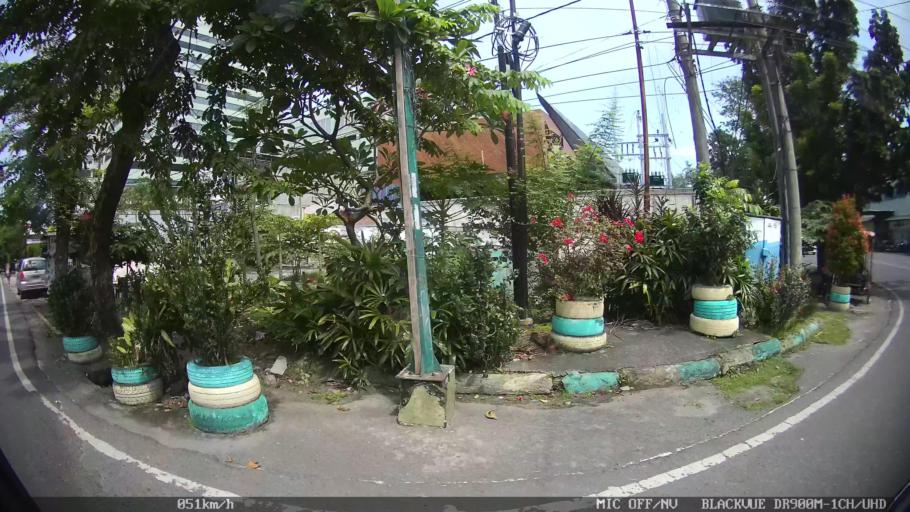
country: ID
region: North Sumatra
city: Medan
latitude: 3.5969
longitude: 98.6768
